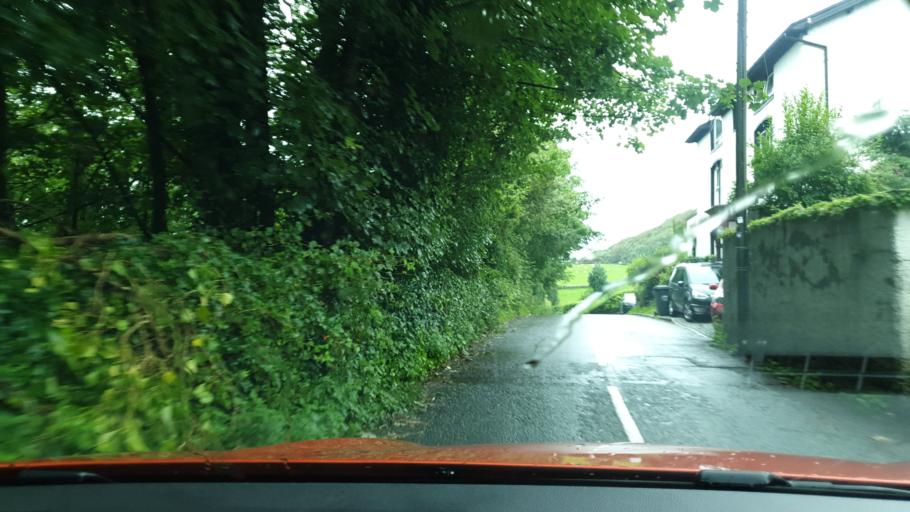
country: GB
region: England
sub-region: Cumbria
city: Ulverston
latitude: 54.2545
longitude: -3.0647
